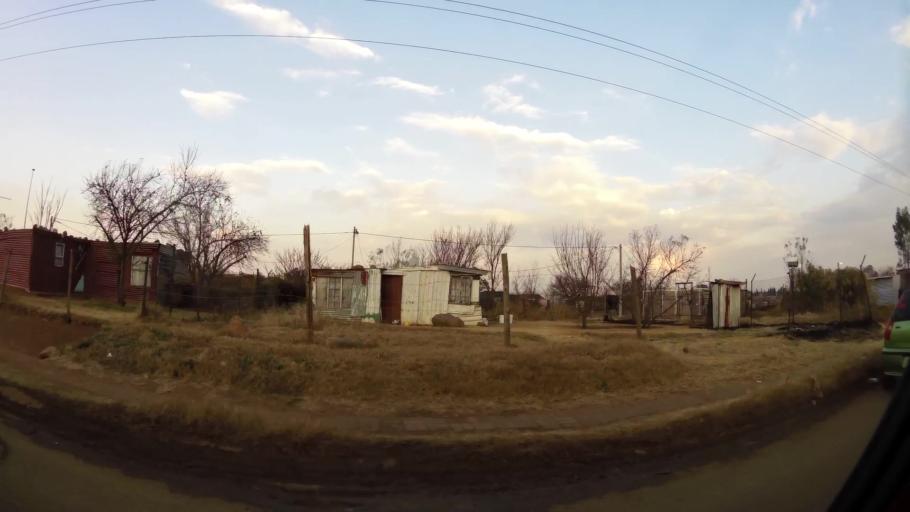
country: ZA
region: Gauteng
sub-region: City of Johannesburg Metropolitan Municipality
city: Orange Farm
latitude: -26.5402
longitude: 27.8447
